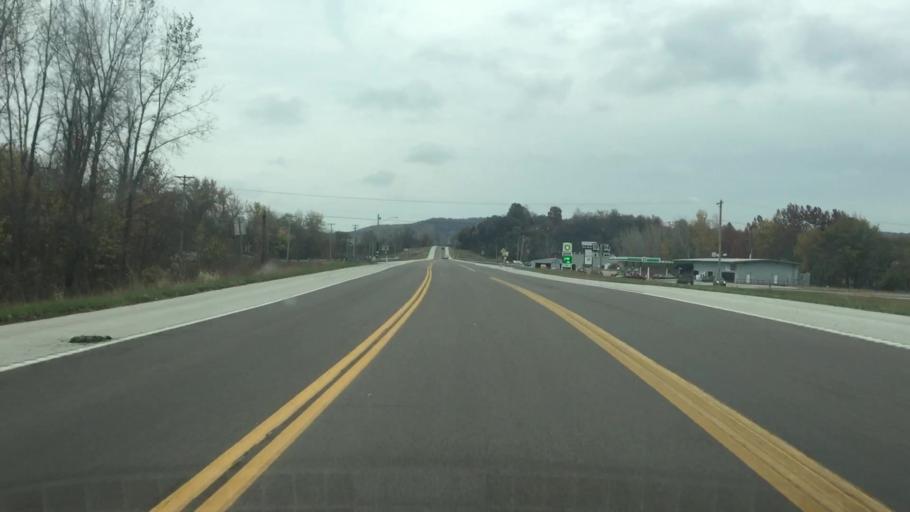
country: US
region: Missouri
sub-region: Gasconade County
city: Hermann
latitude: 38.7277
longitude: -91.4458
